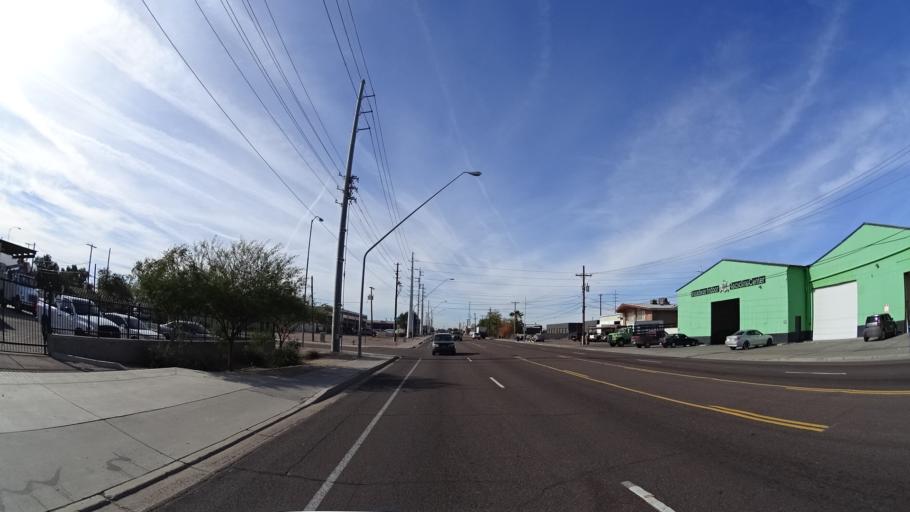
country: US
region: Arizona
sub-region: Maricopa County
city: Mesa
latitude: 33.4078
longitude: -111.8349
